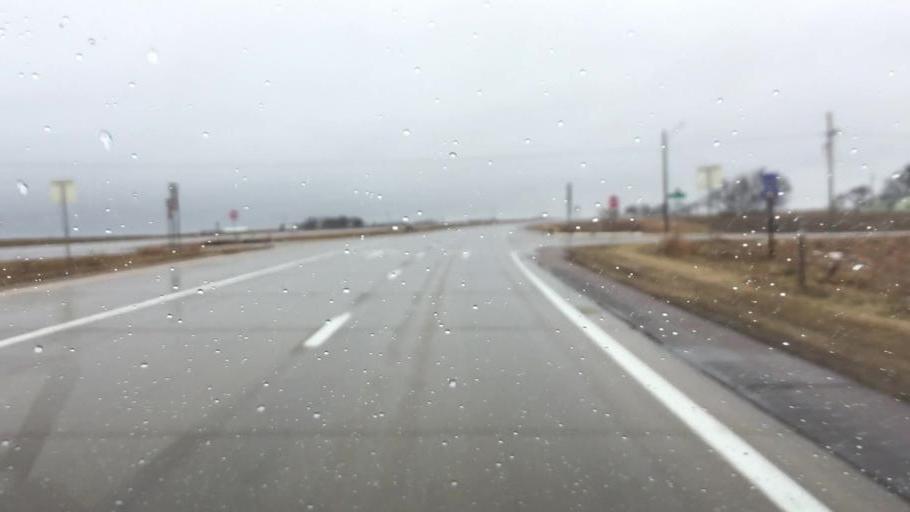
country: US
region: Iowa
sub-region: O'Brien County
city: Sheldon
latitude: 43.0697
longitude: -95.8969
